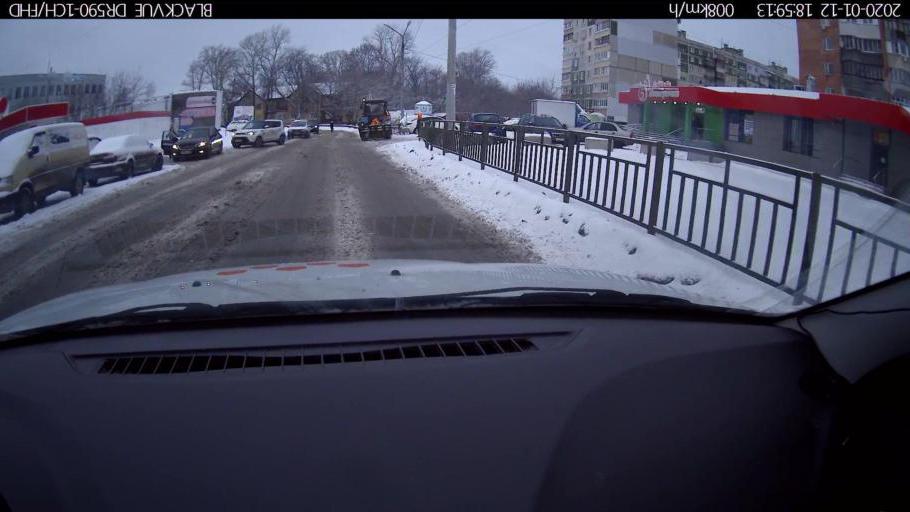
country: RU
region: Nizjnij Novgorod
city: Nizhniy Novgorod
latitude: 56.2757
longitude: 43.9464
